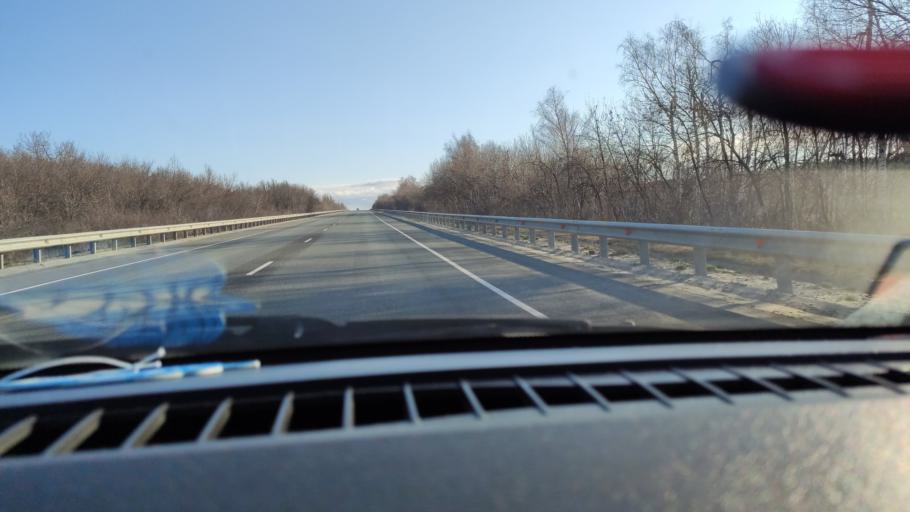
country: RU
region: Saratov
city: Khvalynsk
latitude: 52.6181
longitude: 48.1689
